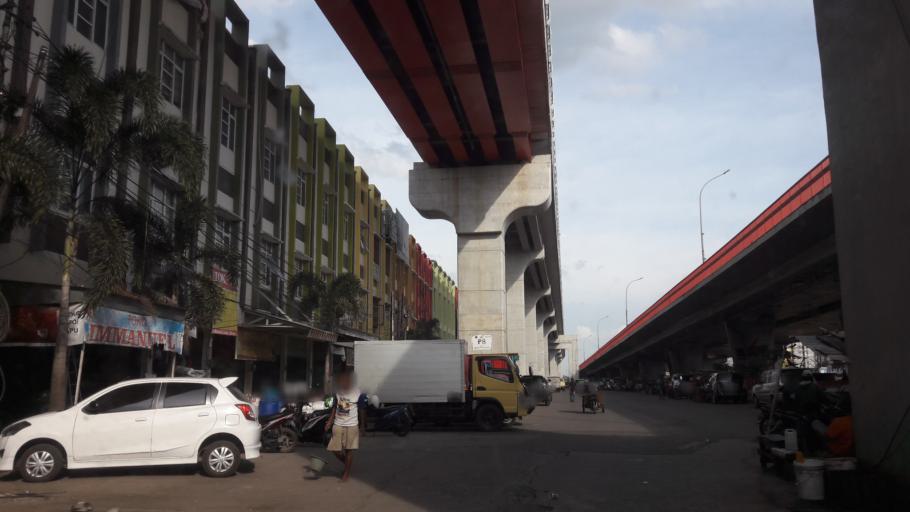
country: ID
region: South Sumatra
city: Plaju
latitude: -2.9929
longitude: 104.7645
